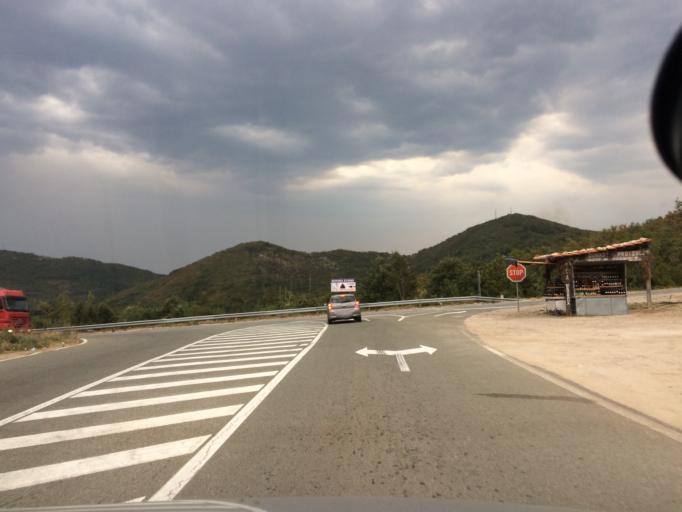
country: ME
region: Opstina Niksic
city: Niksic
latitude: 42.9018
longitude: 18.9603
